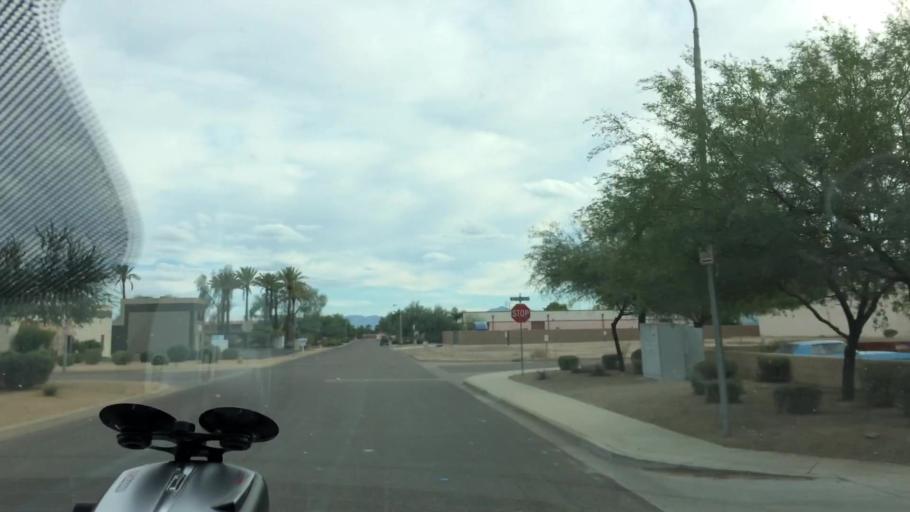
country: US
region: Arizona
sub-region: Maricopa County
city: Peoria
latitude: 33.5647
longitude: -112.2275
